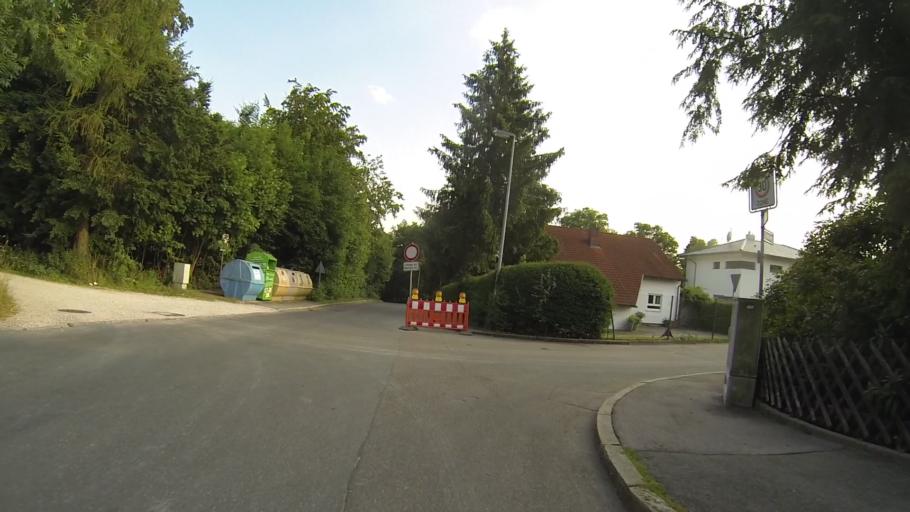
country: DE
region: Baden-Wuerttemberg
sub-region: Tuebingen Region
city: Dornstadt
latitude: 48.4222
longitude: 9.8886
